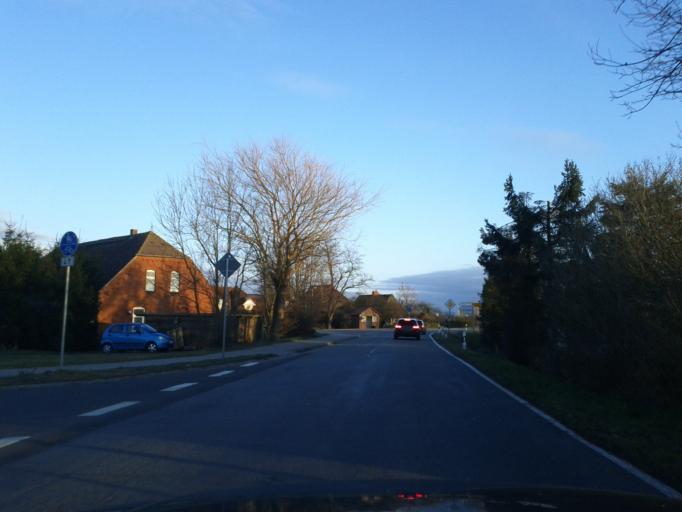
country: DE
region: Mecklenburg-Vorpommern
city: Blowatz
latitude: 53.9744
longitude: 11.4644
